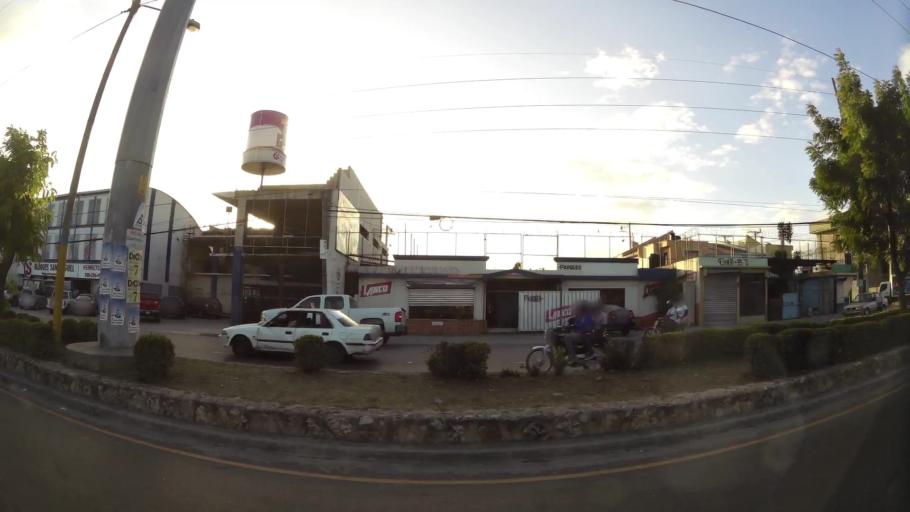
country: DO
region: Santo Domingo
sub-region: Santo Domingo
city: Santo Domingo Este
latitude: 18.4845
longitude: -69.8266
